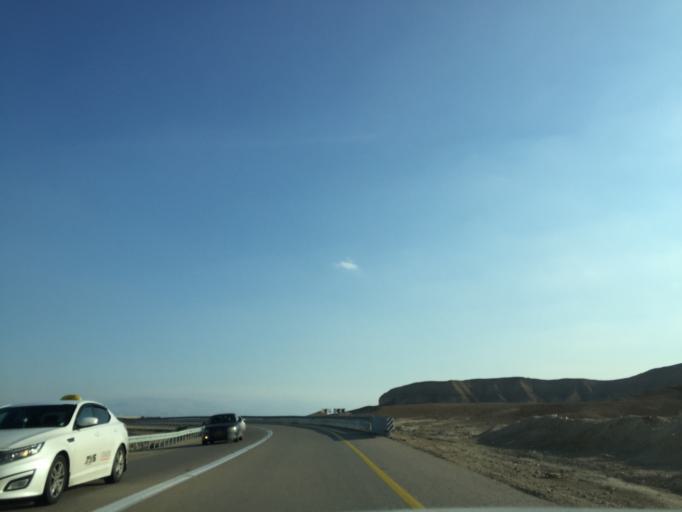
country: IL
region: Southern District
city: `En Boqeq
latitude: 31.1687
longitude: 35.3168
